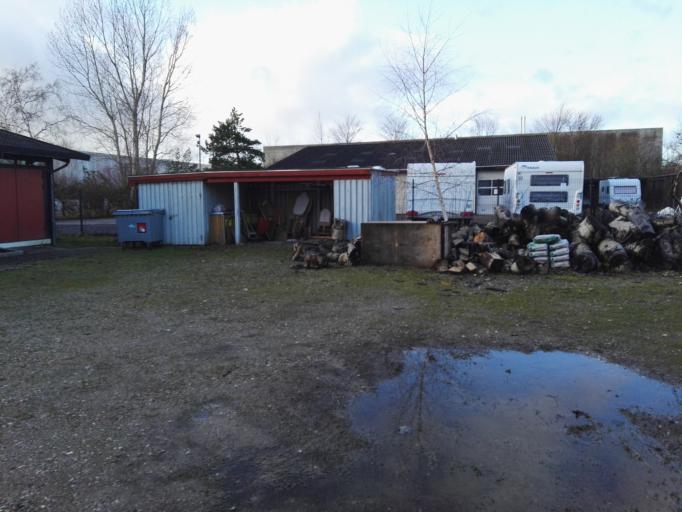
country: DK
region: Capital Region
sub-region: Frederikssund Kommune
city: Frederikssund
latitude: 55.8493
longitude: 12.0763
